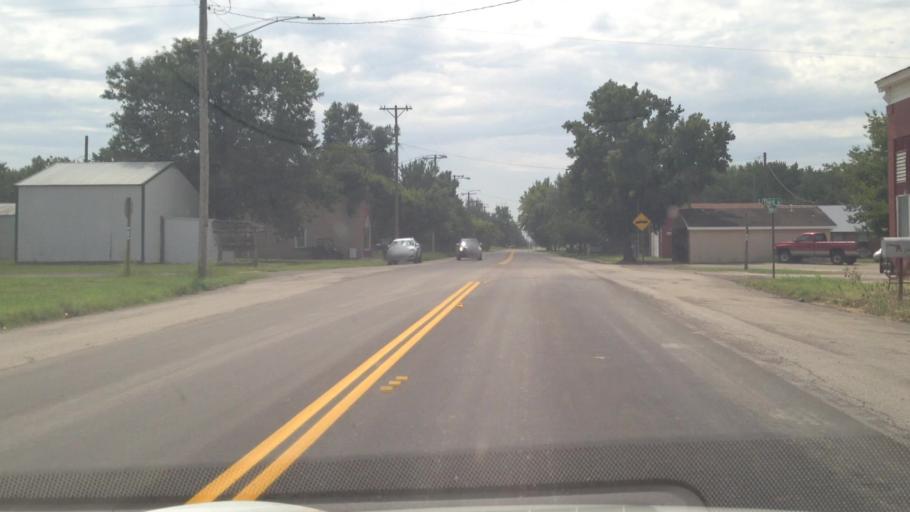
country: US
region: Kansas
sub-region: Crawford County
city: Girard
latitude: 37.6629
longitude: -94.9696
